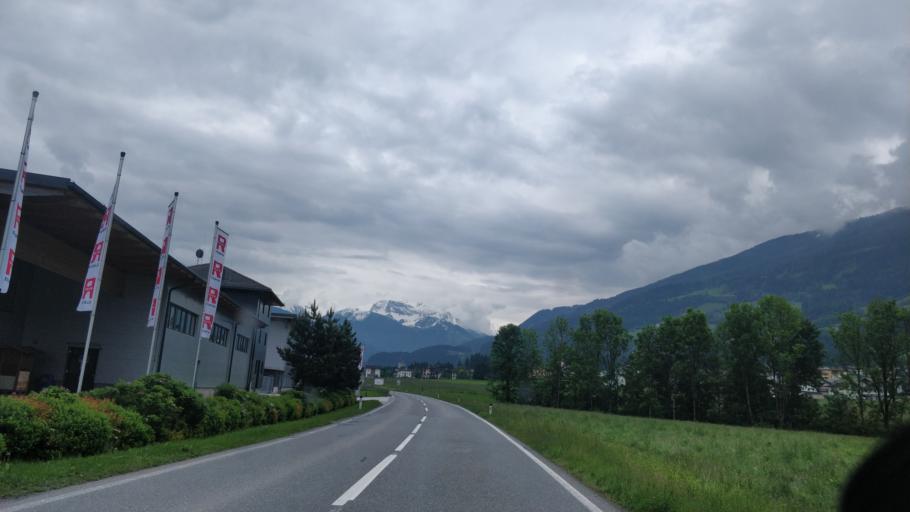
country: AT
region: Tyrol
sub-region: Politischer Bezirk Schwaz
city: Uderns
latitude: 47.3085
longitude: 11.8679
